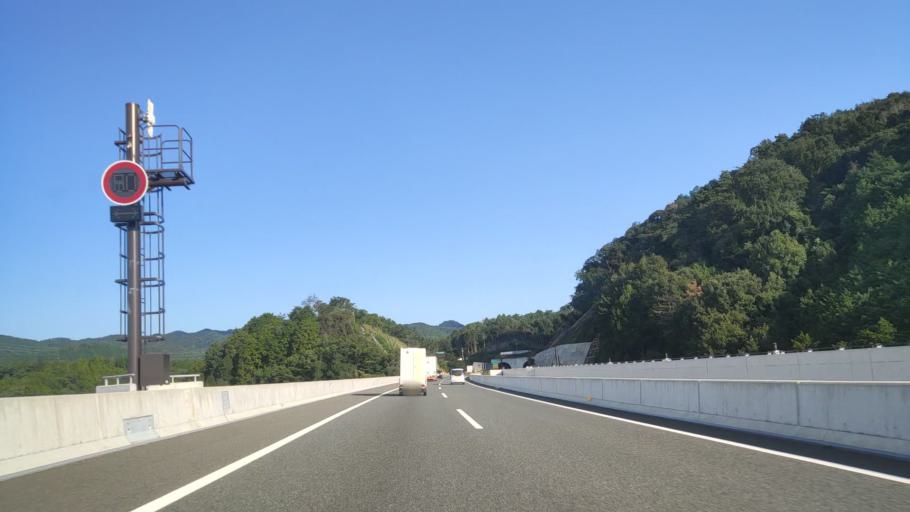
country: JP
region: Osaka
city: Takatsuki
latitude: 34.8904
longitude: 135.6106
